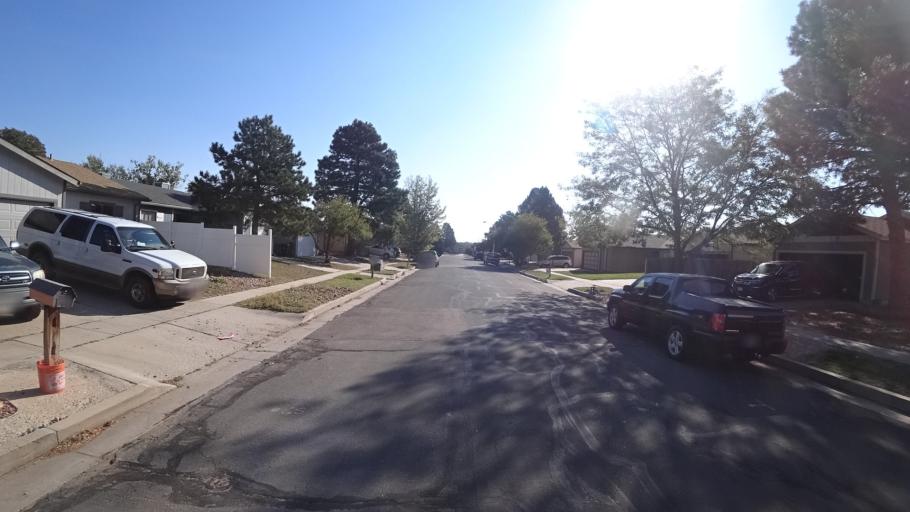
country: US
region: Colorado
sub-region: El Paso County
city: Cimarron Hills
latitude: 38.8802
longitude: -104.7223
